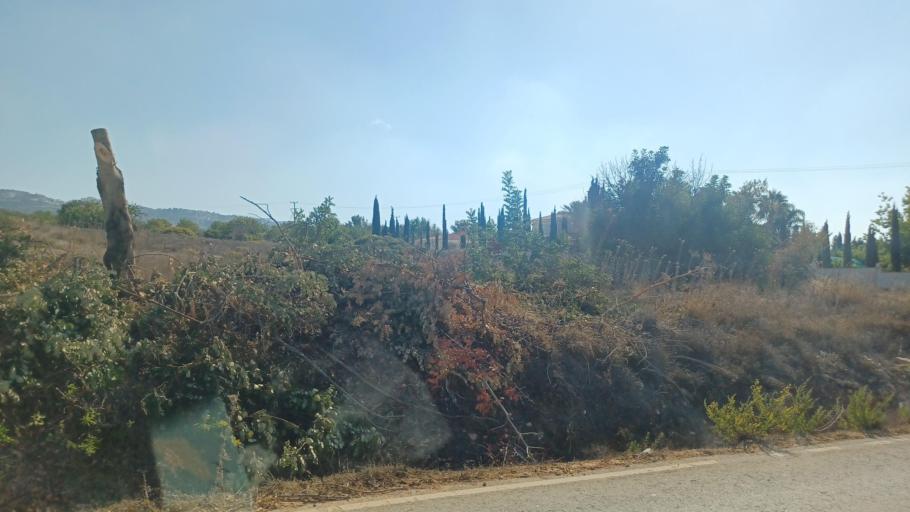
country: CY
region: Pafos
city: Tala
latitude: 34.8296
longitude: 32.4463
